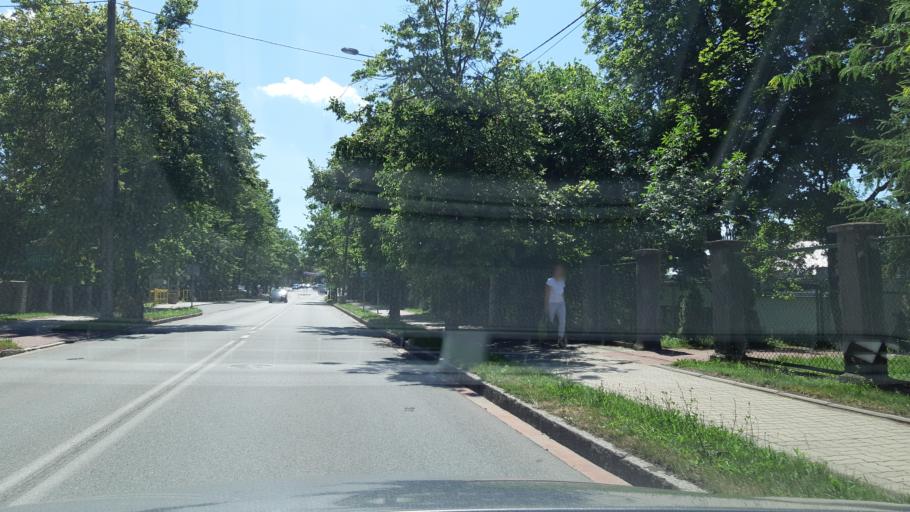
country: PL
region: Warmian-Masurian Voivodeship
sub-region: Powiat mragowski
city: Mragowo
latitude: 53.8793
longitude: 21.3034
